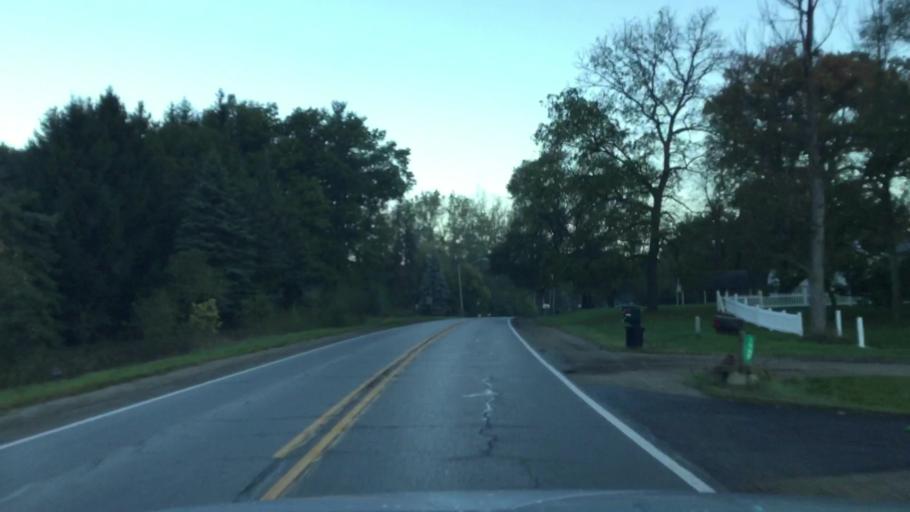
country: US
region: Michigan
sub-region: Livingston County
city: Howell
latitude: 42.6281
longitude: -83.9291
